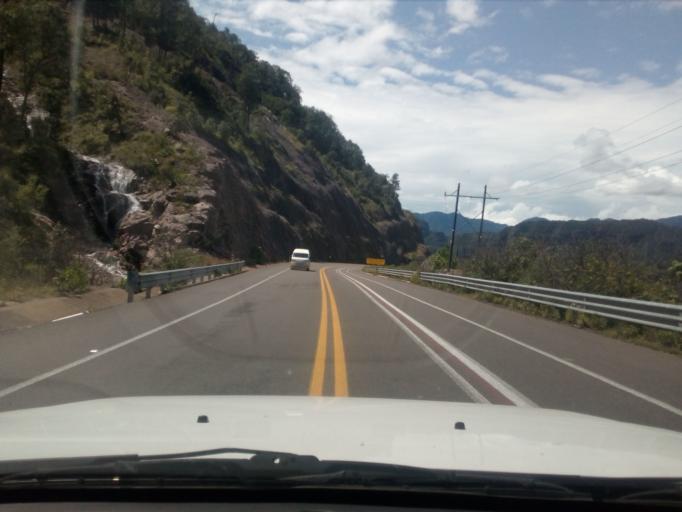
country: MX
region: Durango
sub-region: Pueblo Nuevo
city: La Ciudad
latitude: 23.6221
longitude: -105.6860
